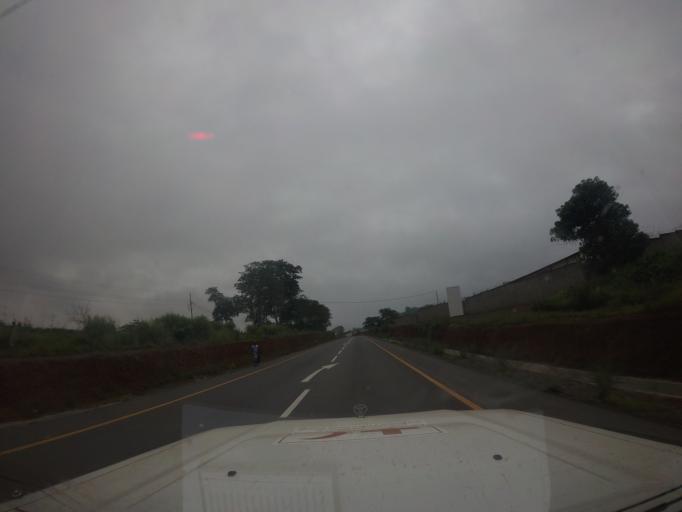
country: SL
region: Eastern Province
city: Hangha
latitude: 7.9225
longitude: -11.1543
